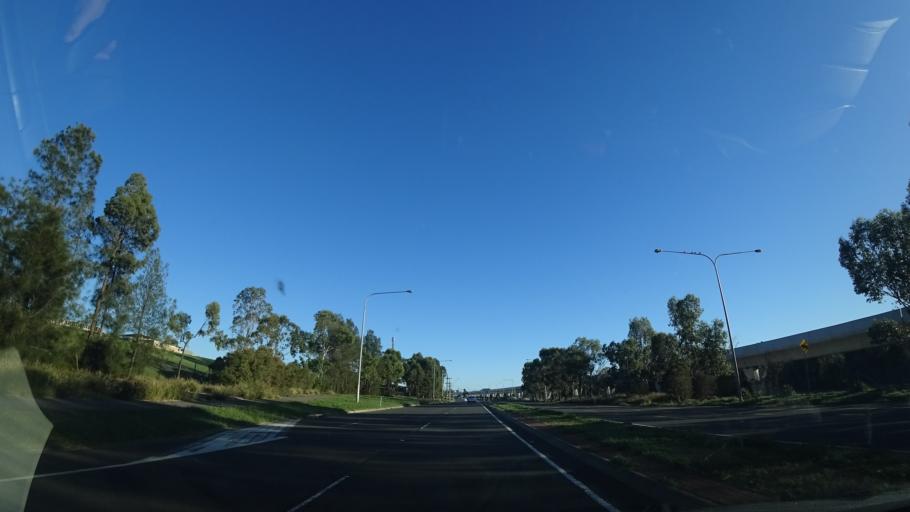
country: AU
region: New South Wales
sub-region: Blacktown
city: Stanhope Gardens
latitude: -33.7064
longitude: 150.9308
